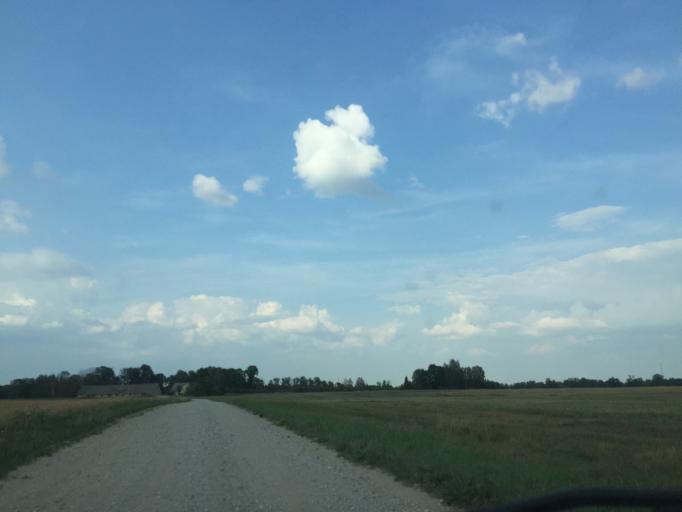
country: LT
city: Zagare
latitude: 56.4801
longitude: 23.1486
